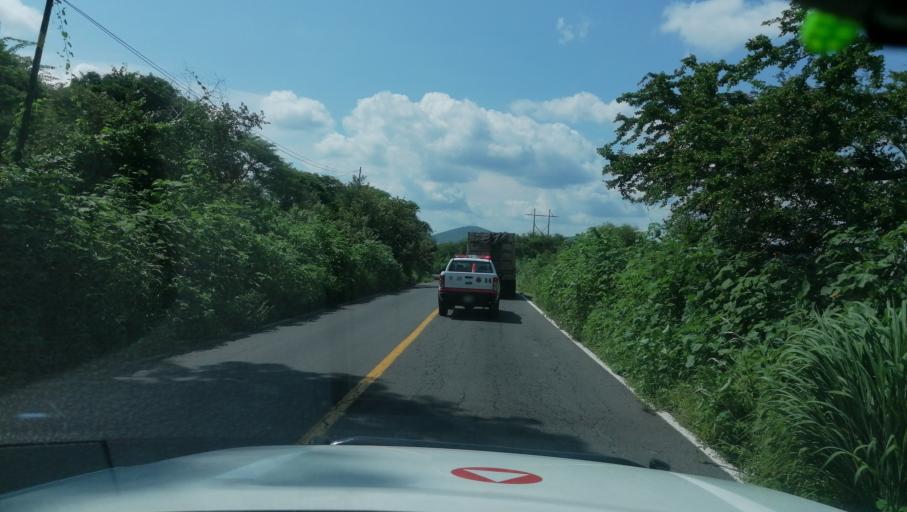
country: MX
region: Morelos
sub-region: Tepalcingo
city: Zacapalco
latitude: 18.6499
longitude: -98.9705
